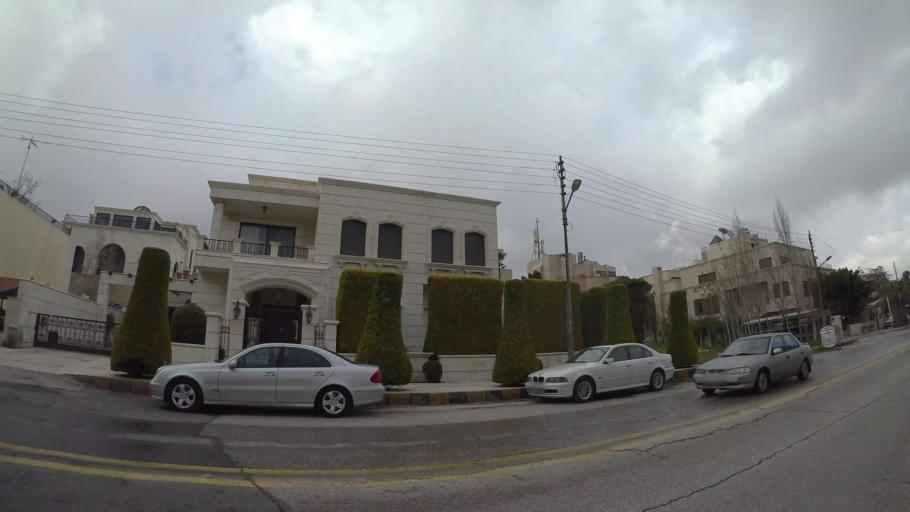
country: JO
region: Amman
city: Al Bunayyat ash Shamaliyah
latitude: 31.9461
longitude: 35.8895
